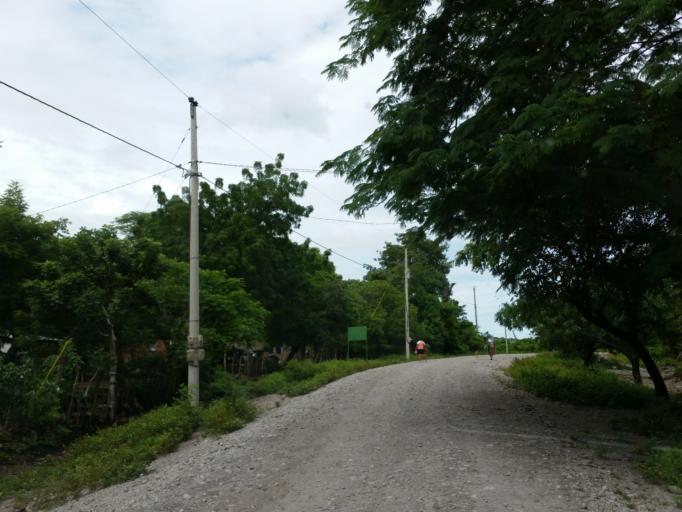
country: NI
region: Leon
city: Telica
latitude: 12.6981
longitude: -86.8680
